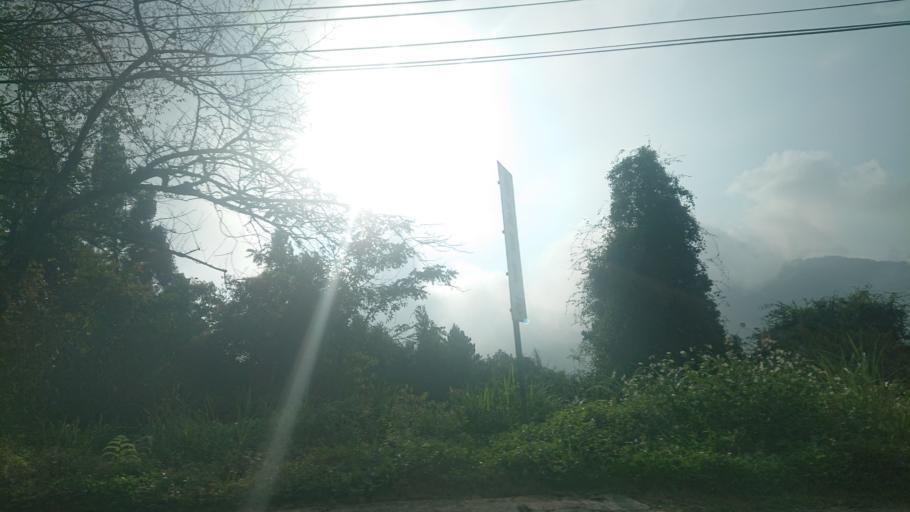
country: TW
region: Taiwan
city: Lugu
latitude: 23.4947
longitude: 120.7927
